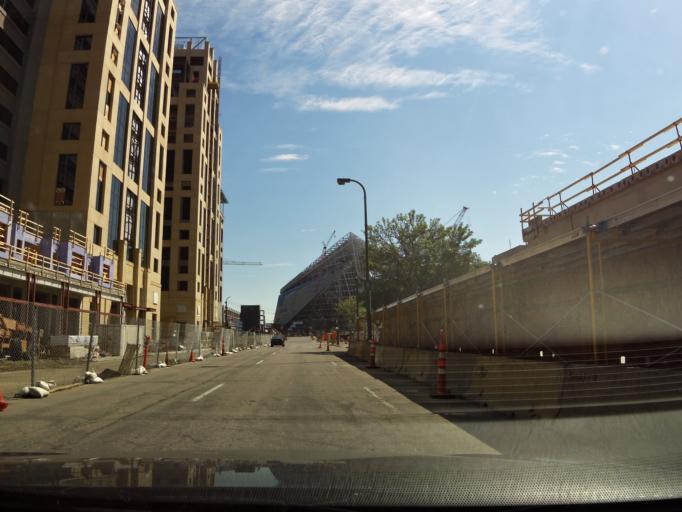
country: US
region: Minnesota
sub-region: Hennepin County
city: Minneapolis
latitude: 44.9768
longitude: -93.2629
